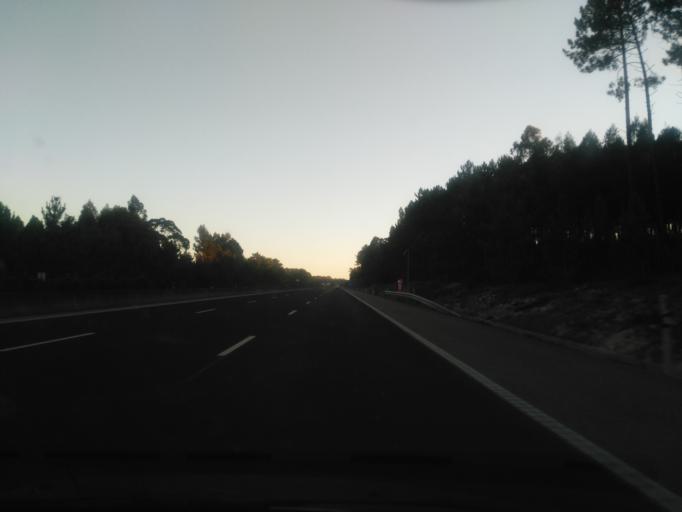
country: PT
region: Leiria
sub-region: Leiria
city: Maceira
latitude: 39.7082
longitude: -8.9183
